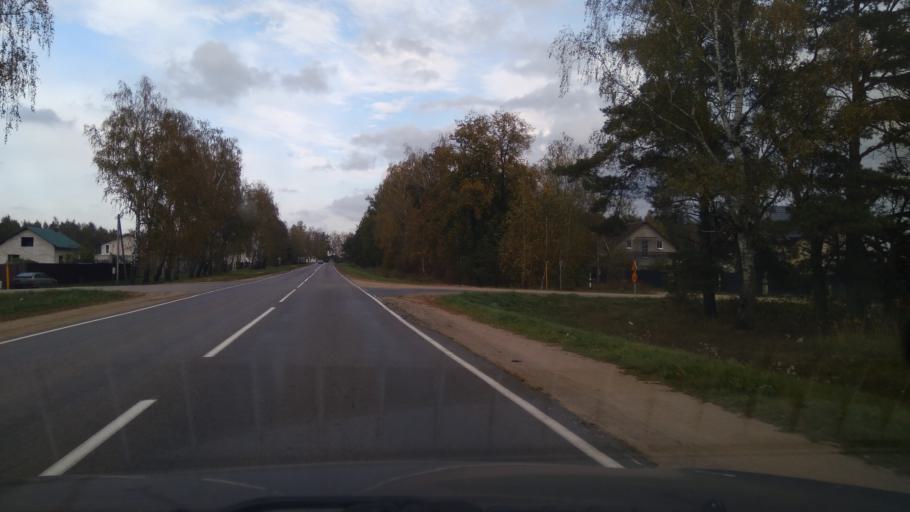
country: BY
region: Minsk
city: Svislach
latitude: 53.6510
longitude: 27.9289
